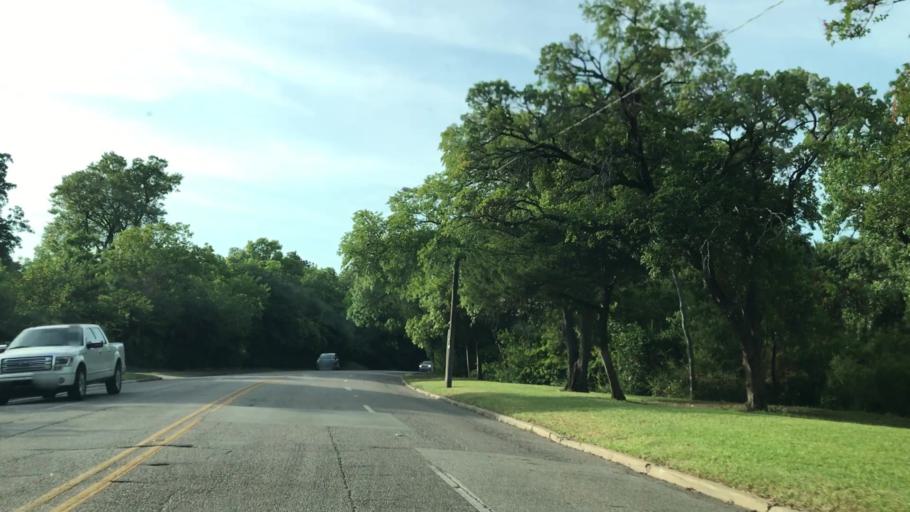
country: US
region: Texas
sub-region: Dallas County
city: Highland Park
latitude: 32.8177
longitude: -96.7996
